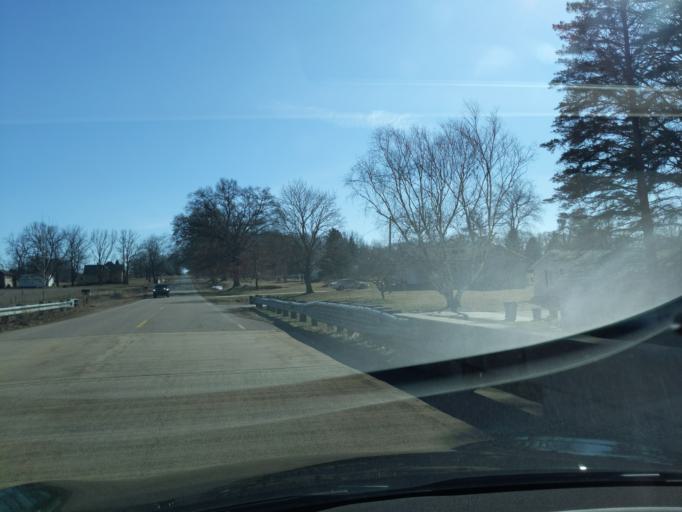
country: US
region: Michigan
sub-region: Ingham County
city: Leslie
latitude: 42.4036
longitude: -84.4434
